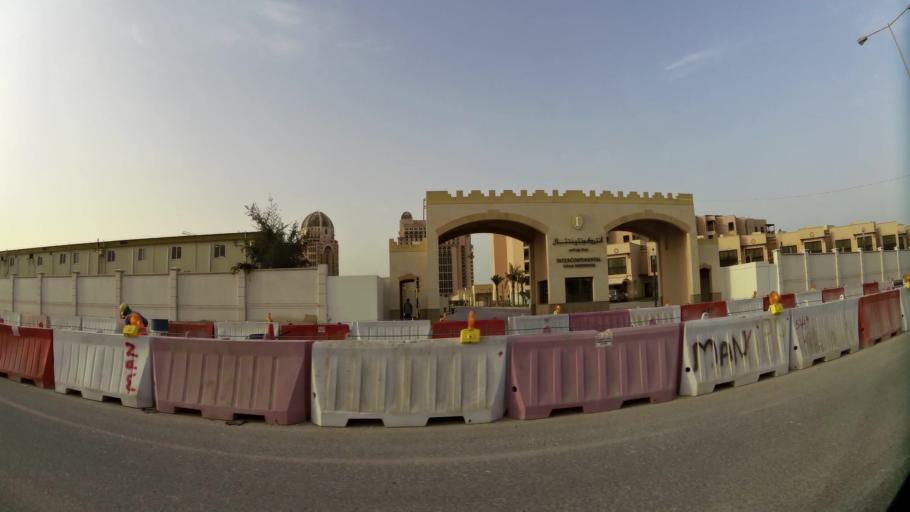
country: QA
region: Baladiyat ad Dawhah
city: Doha
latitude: 25.3462
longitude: 51.5281
